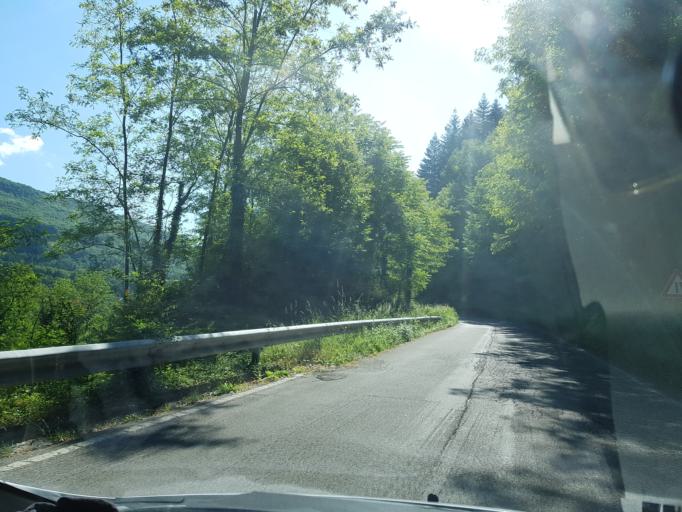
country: IT
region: Tuscany
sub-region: Provincia di Lucca
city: Camporgiano
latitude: 44.1684
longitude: 10.3249
